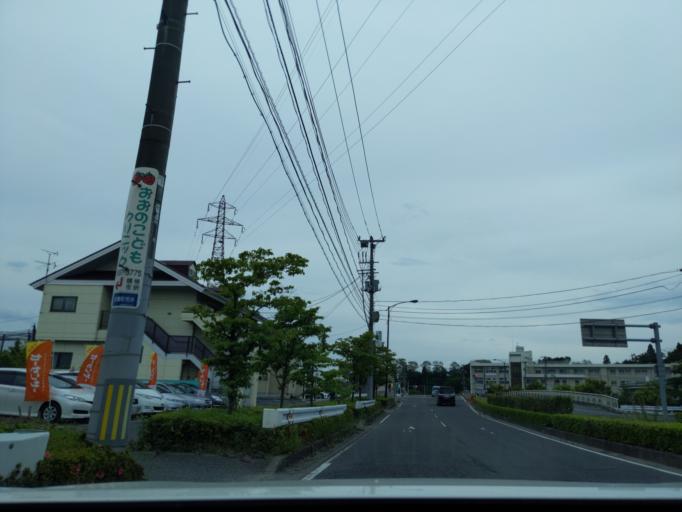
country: JP
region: Fukushima
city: Koriyama
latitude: 37.3672
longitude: 140.3627
